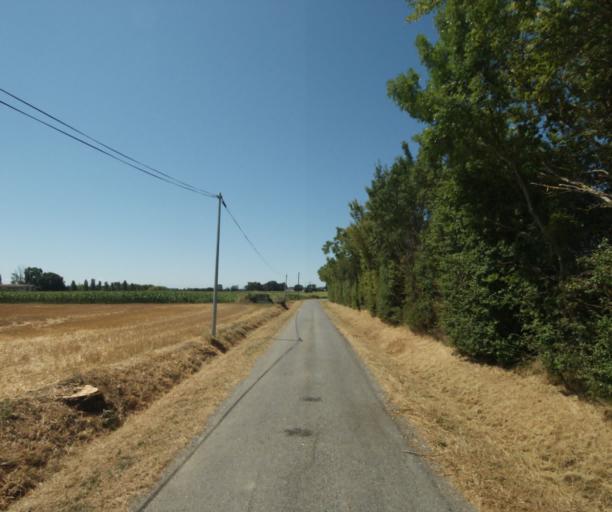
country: FR
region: Midi-Pyrenees
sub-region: Departement de la Haute-Garonne
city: Revel
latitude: 43.4979
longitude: 1.9555
